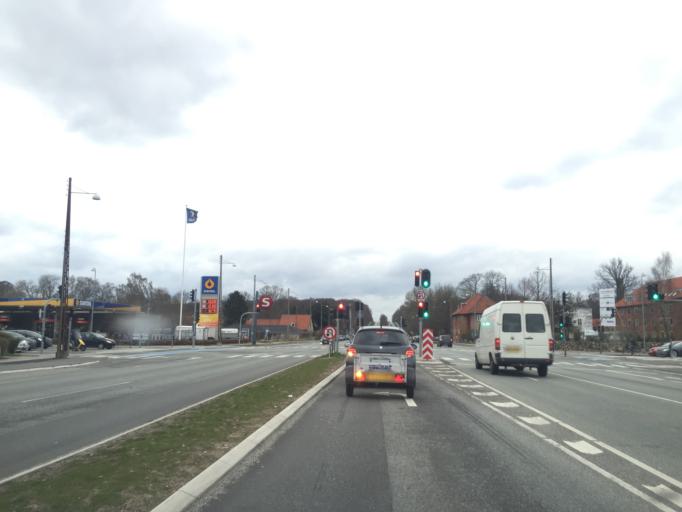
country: DK
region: Capital Region
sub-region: Rudersdal Kommune
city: Holte
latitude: 55.7967
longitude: 12.4822
